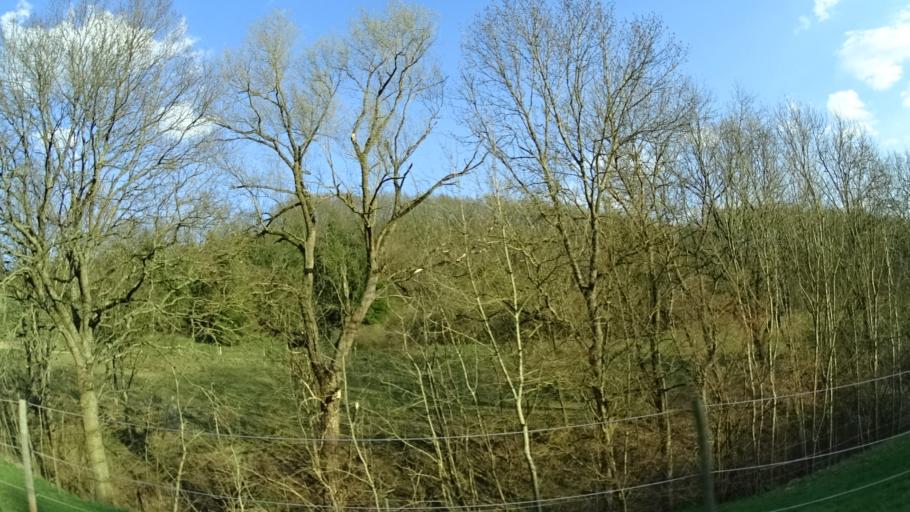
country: DE
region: Rheinland-Pfalz
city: Lettweiler
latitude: 49.7326
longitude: 7.7164
